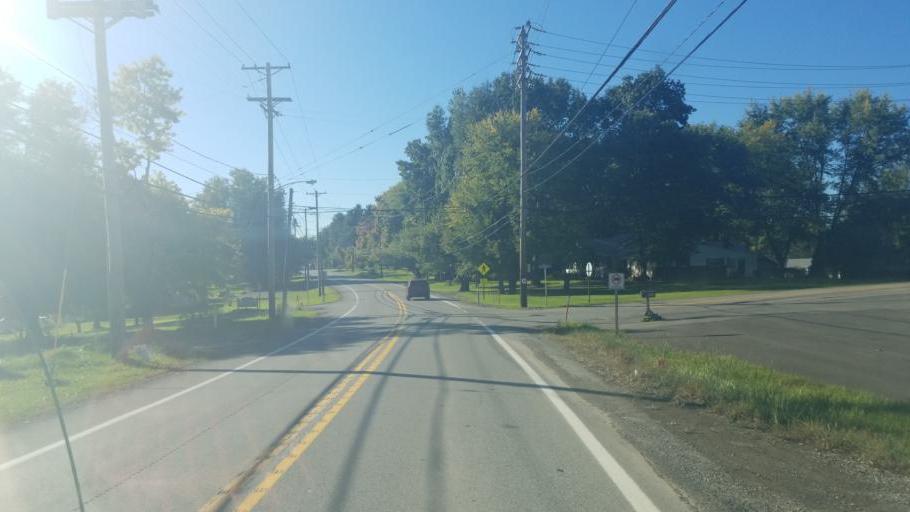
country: US
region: Pennsylvania
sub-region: Allegheny County
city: Imperial
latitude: 40.4930
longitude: -80.3006
